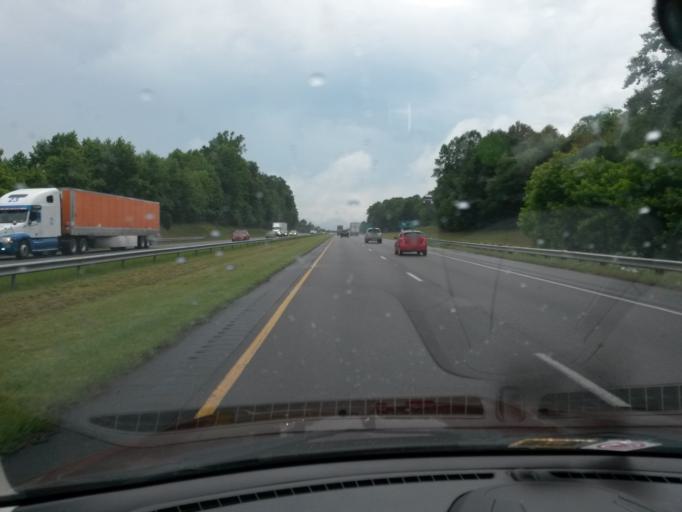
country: US
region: North Carolina
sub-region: Catawba County
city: Claremont
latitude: 35.7403
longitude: -81.0854
